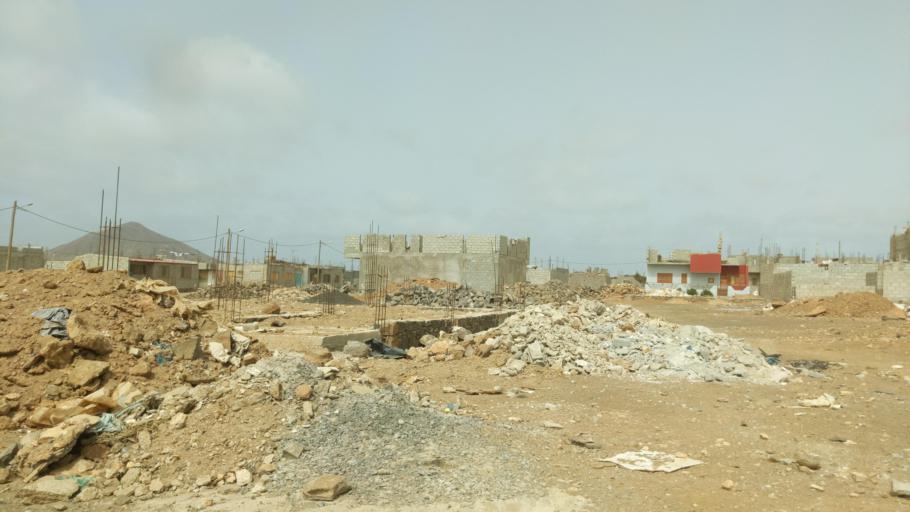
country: CV
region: Sal
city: Espargos
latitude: 16.7673
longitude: -22.9448
